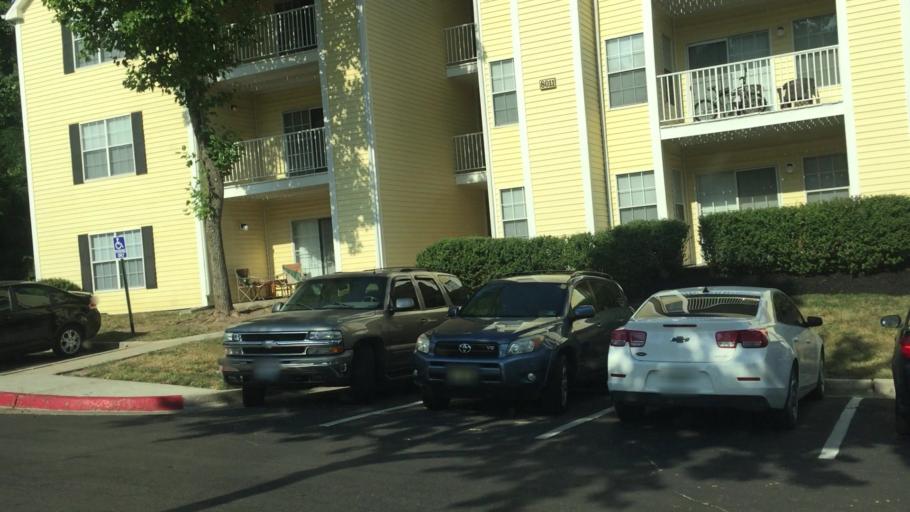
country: US
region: Missouri
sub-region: Clay County
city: Gladstone
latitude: 39.2396
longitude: -94.5932
